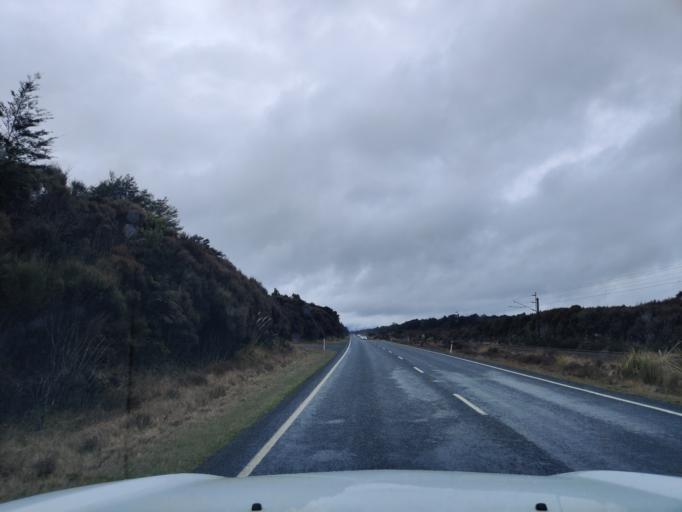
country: NZ
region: Manawatu-Wanganui
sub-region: Ruapehu District
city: Waiouru
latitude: -39.3227
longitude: 175.3853
